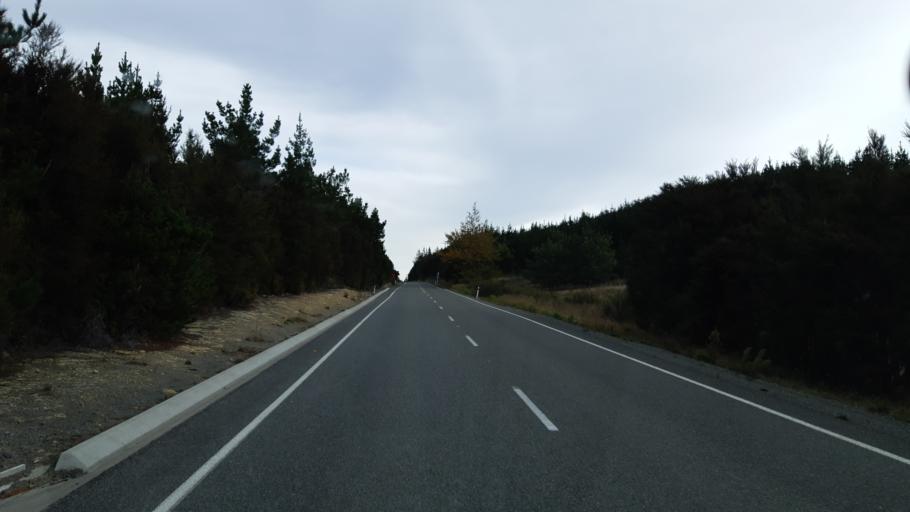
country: NZ
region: Tasman
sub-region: Tasman District
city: Brightwater
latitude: -41.6585
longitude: 173.2273
